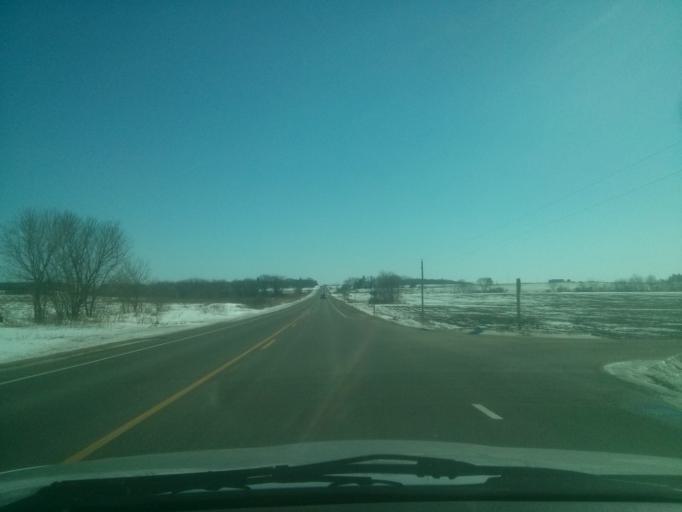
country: US
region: Wisconsin
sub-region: Polk County
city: Clear Lake
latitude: 45.1364
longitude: -92.3332
